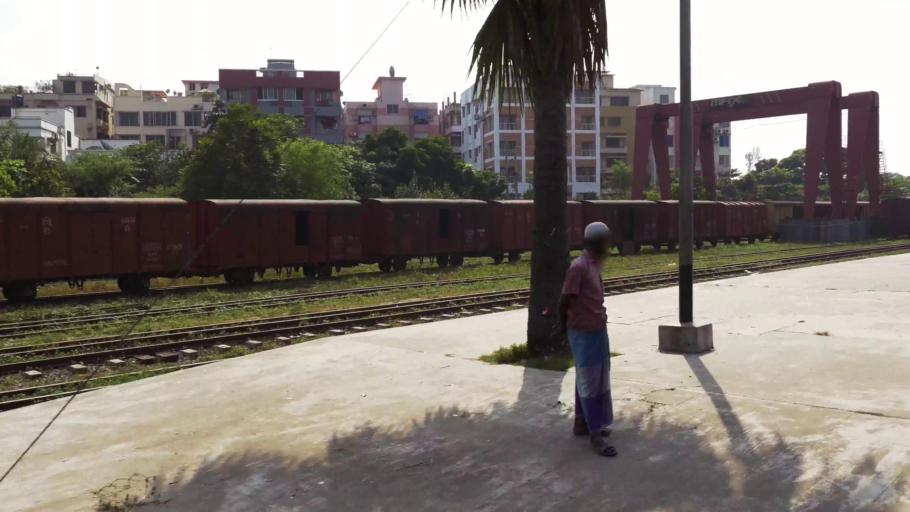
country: BD
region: Dhaka
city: Tungi
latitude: 23.8675
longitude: 90.4061
